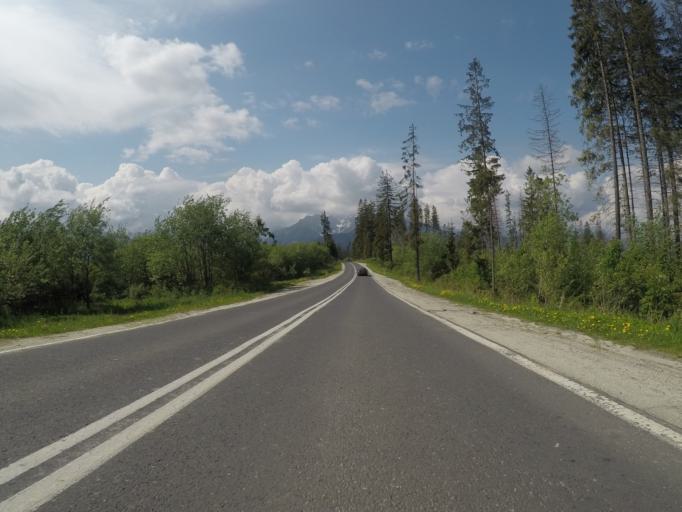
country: PL
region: Lesser Poland Voivodeship
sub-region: Powiat tatrzanski
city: Bukowina Tatrzanska
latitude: 49.2995
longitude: 20.1175
